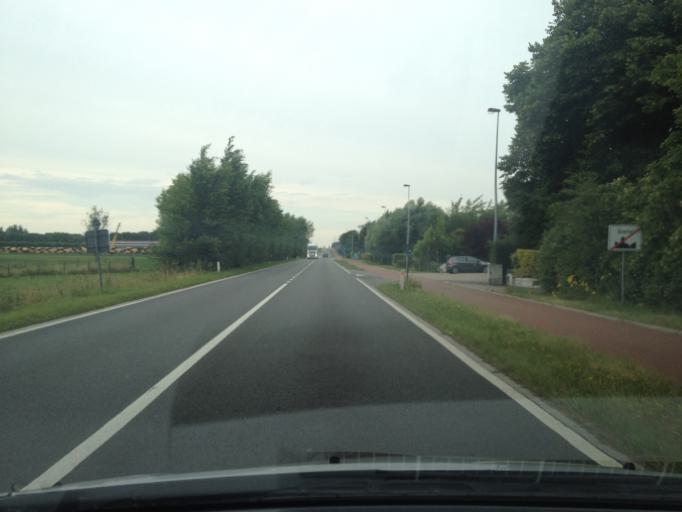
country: BE
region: Flanders
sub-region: Provincie West-Vlaanderen
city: Gistel
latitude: 51.1545
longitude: 2.9458
